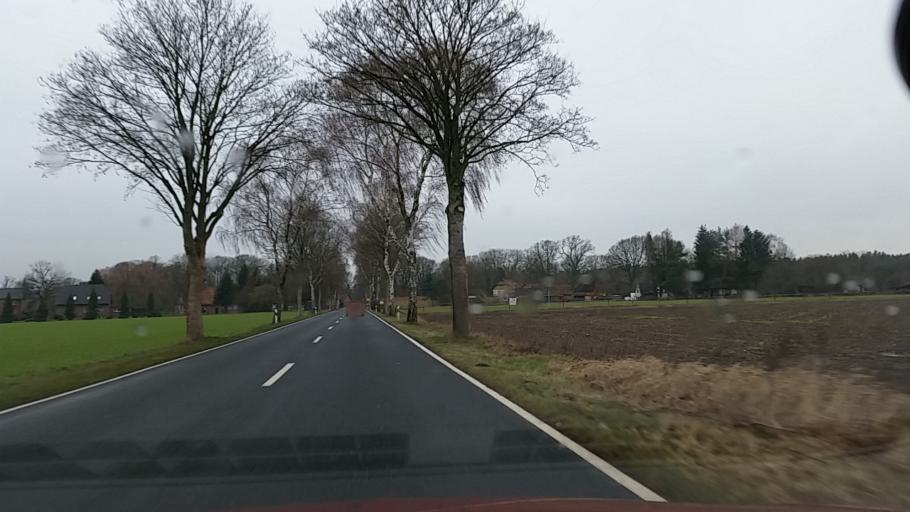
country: DE
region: Lower Saxony
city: Sprakensehl
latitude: 52.7695
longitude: 10.4615
